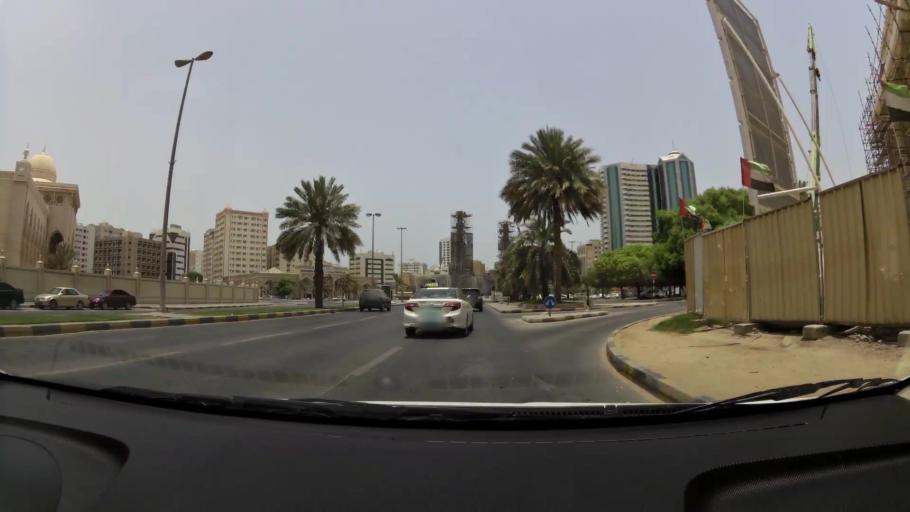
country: AE
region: Ash Shariqah
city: Sharjah
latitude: 25.3517
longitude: 55.3925
